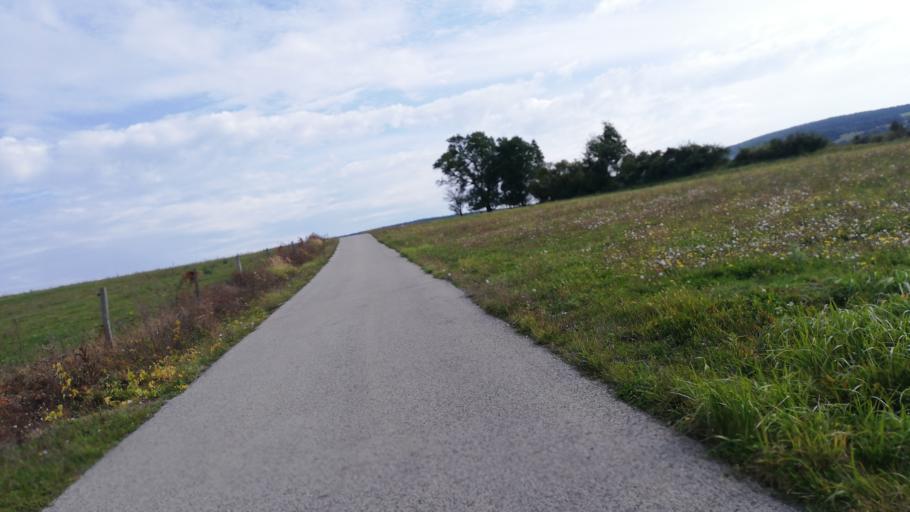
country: CZ
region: South Moravian
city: Sudomerice
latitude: 48.8410
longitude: 17.2871
